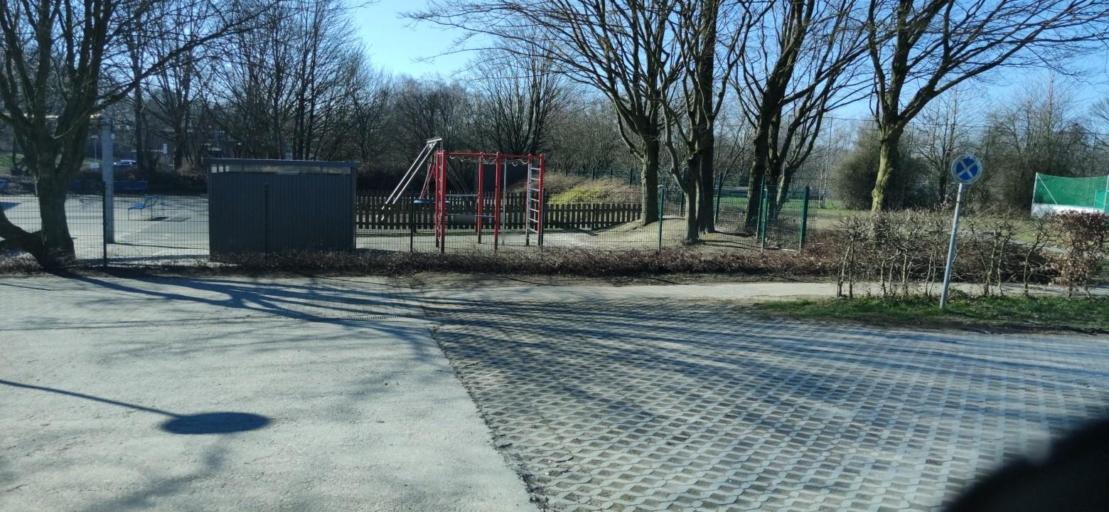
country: DE
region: North Rhine-Westphalia
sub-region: Regierungsbezirk Dusseldorf
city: Mettmann
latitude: 51.2380
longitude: 7.0011
